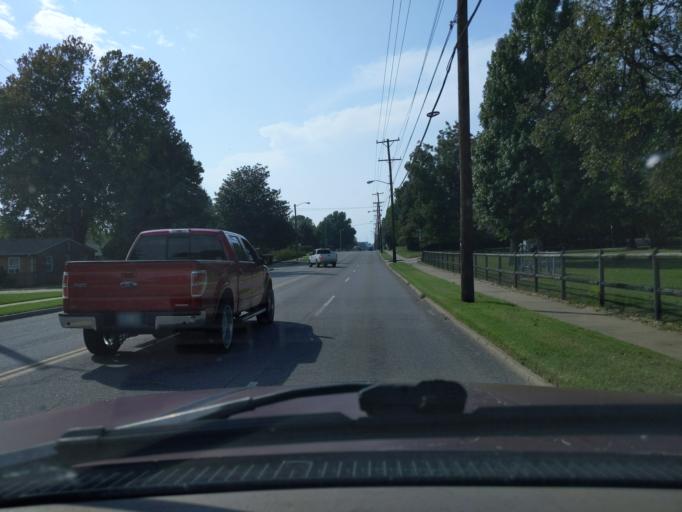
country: US
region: Oklahoma
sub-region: Tulsa County
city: Tulsa
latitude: 36.1333
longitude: -95.9430
